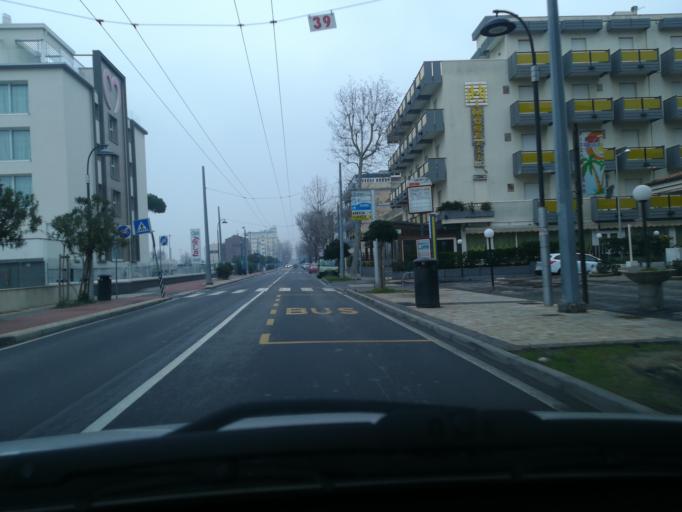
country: IT
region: Emilia-Romagna
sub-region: Provincia di Rimini
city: Riccione
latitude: 44.0181
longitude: 12.6391
